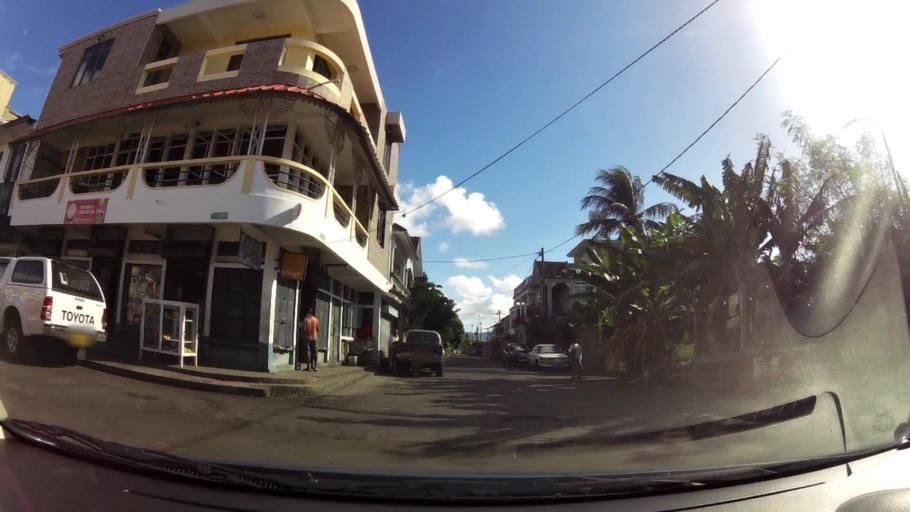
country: MU
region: Grand Port
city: Mahebourg
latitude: -20.4062
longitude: 57.7058
